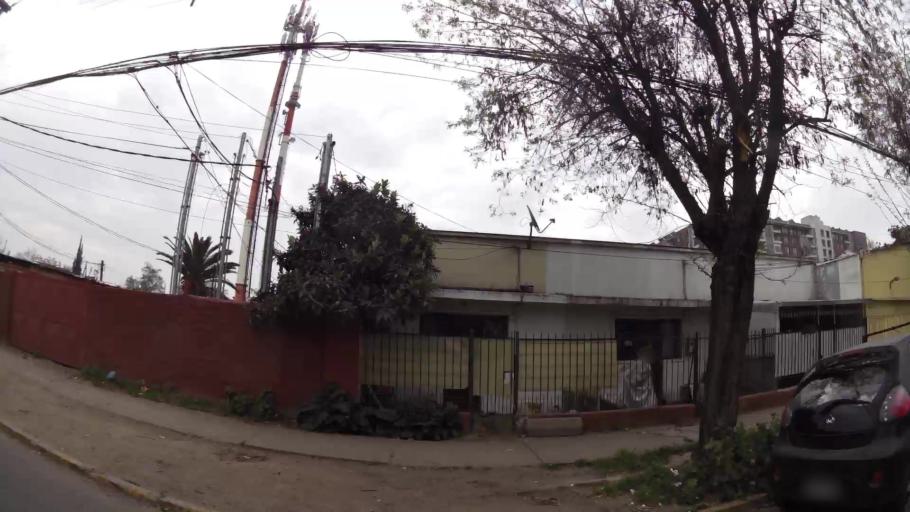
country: CL
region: Santiago Metropolitan
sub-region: Provincia de Santiago
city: Villa Presidente Frei, Nunoa, Santiago, Chile
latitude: -33.4800
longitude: -70.5965
